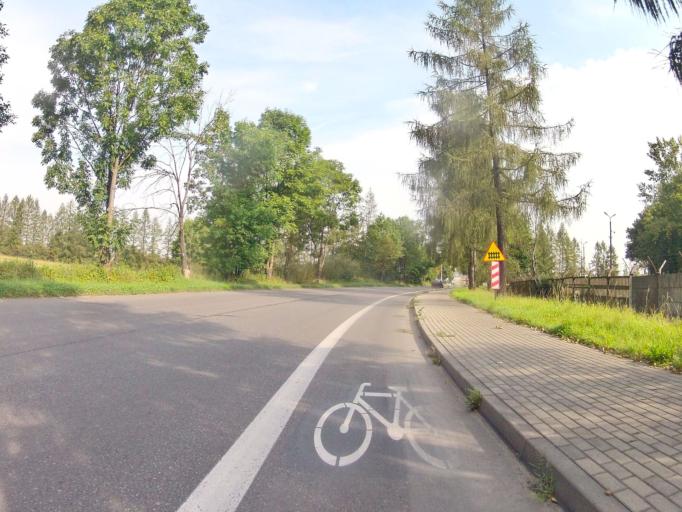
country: PL
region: Subcarpathian Voivodeship
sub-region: Powiat jasielski
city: Jaslo
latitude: 49.7243
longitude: 21.4490
